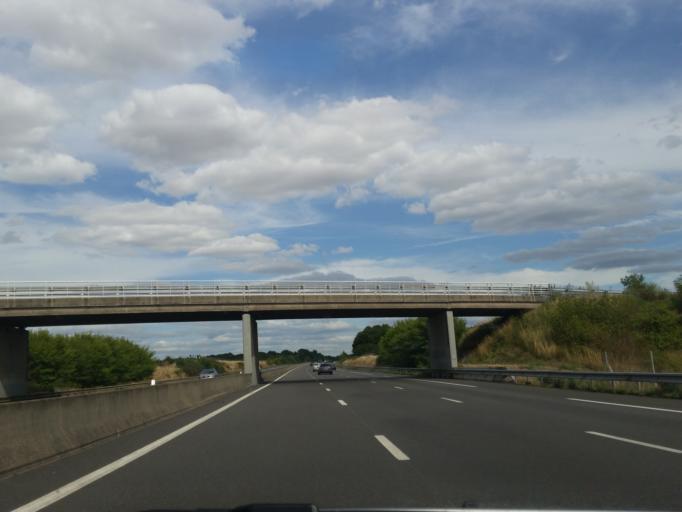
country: FR
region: Centre
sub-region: Departement du Loir-et-Cher
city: Saint-Sulpice-de-Pommeray
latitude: 47.6177
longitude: 1.2185
